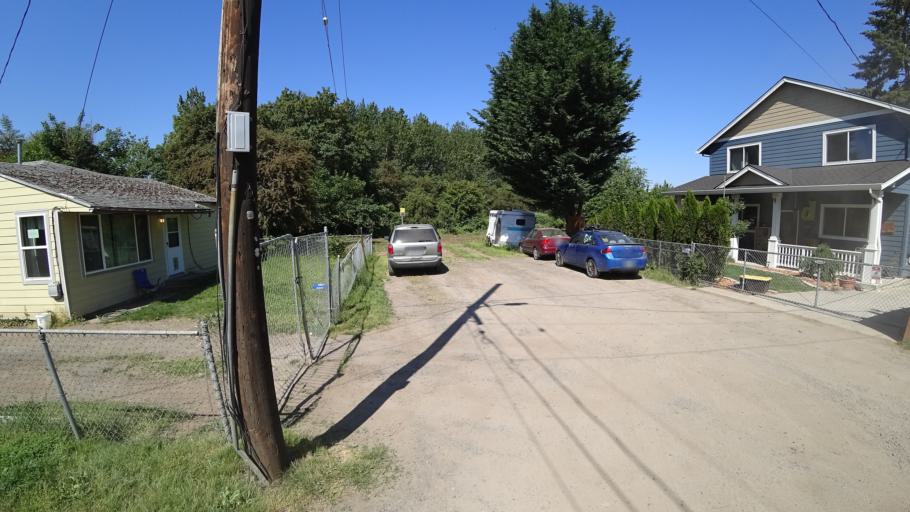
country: US
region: Oregon
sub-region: Multnomah County
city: Lents
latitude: 45.4805
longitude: -122.5460
